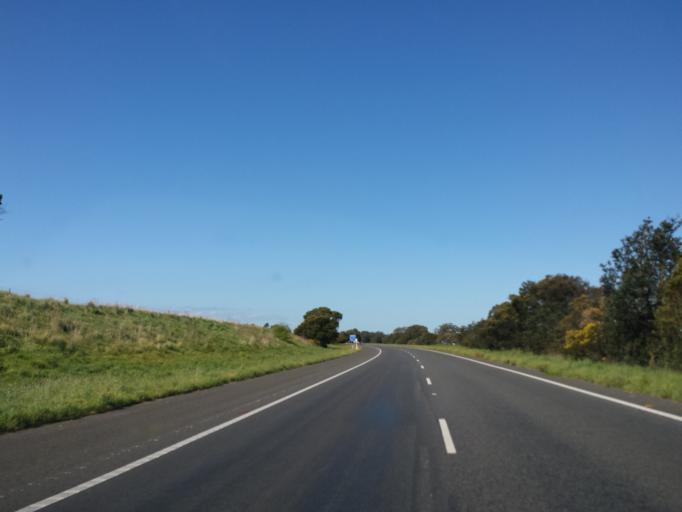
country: AU
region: Victoria
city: Brown Hill
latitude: -37.5526
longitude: 144.0092
